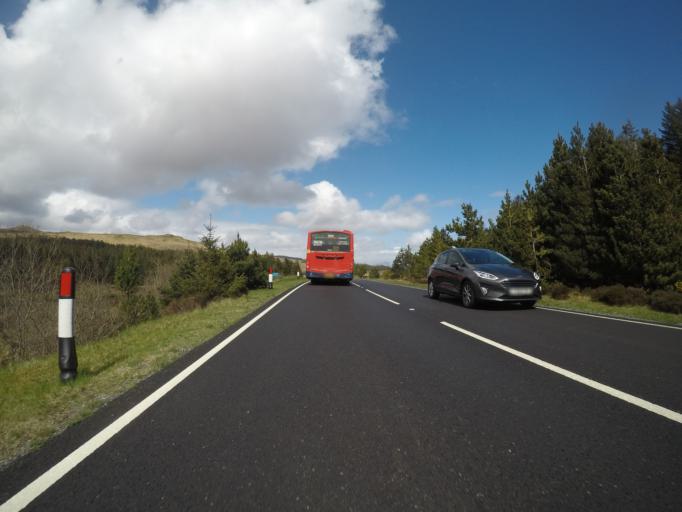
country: GB
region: Scotland
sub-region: Highland
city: Isle of Skye
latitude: 57.3282
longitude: -6.2029
